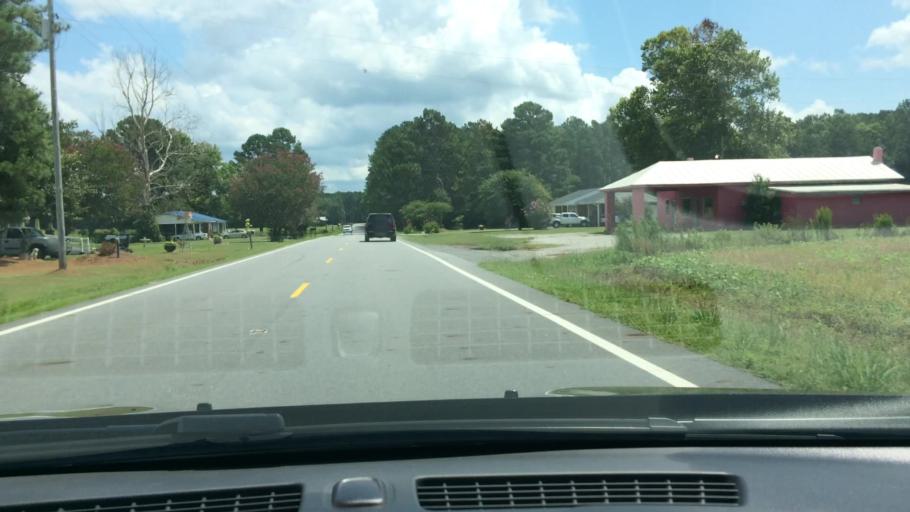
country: US
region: North Carolina
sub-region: Craven County
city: Vanceboro
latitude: 35.4213
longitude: -77.2293
